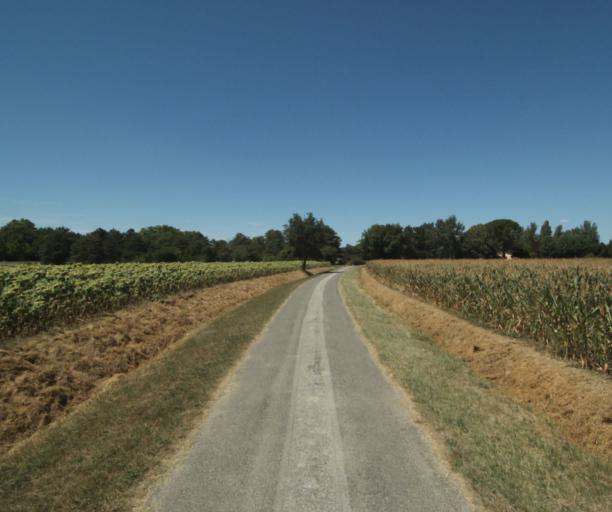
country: FR
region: Midi-Pyrenees
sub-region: Departement de la Haute-Garonne
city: Revel
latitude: 43.4779
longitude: 1.9467
